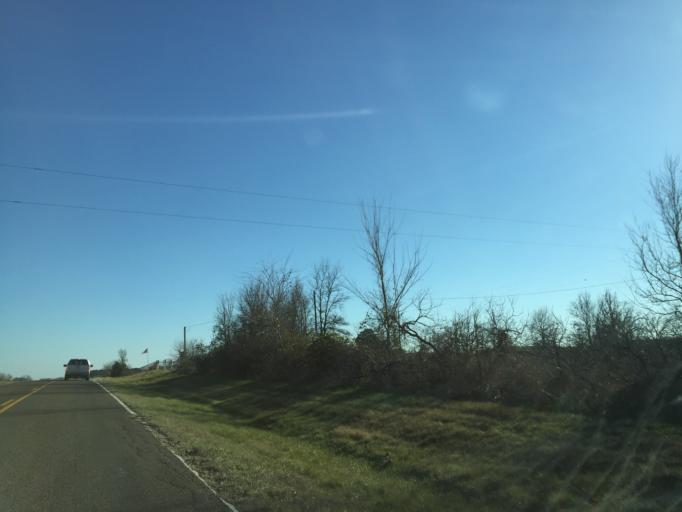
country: US
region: Texas
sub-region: Bastrop County
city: Elgin
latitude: 30.4141
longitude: -97.2552
